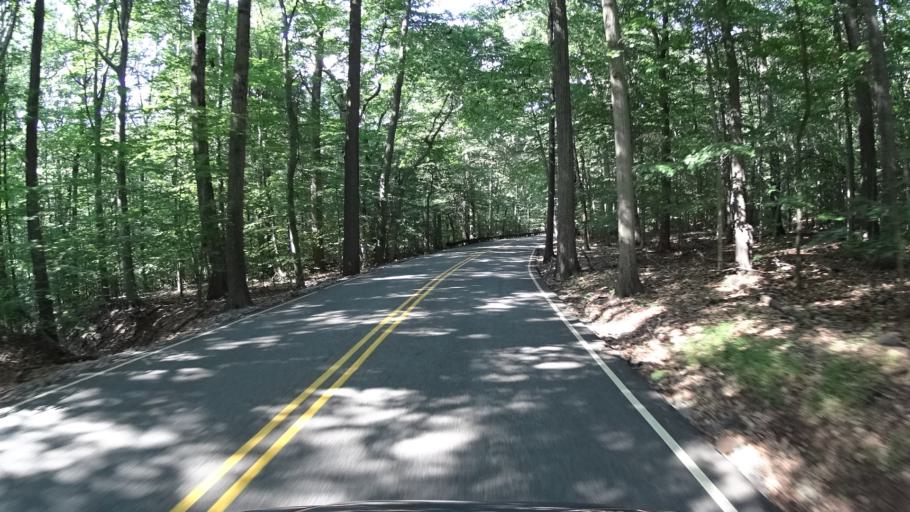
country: US
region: New Jersey
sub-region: Union County
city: Mountainside
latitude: 40.6906
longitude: -74.3717
